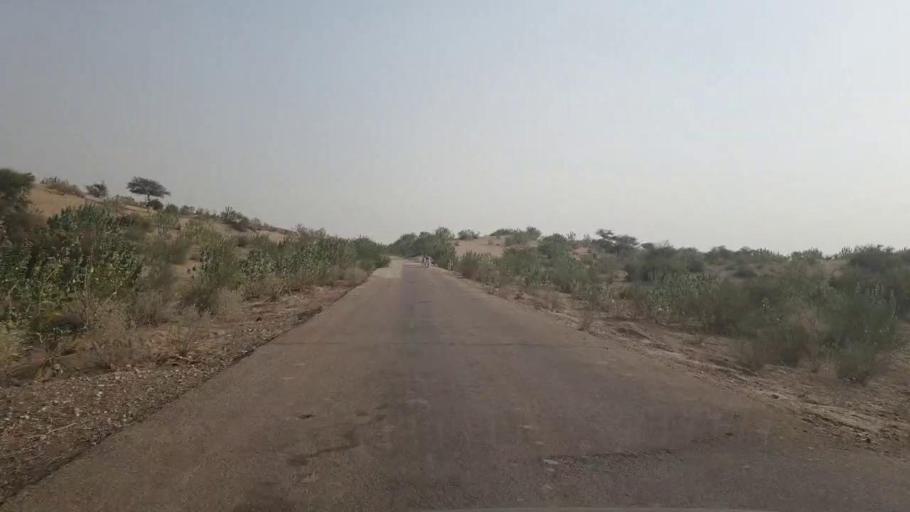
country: PK
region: Sindh
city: Chor
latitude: 25.5303
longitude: 69.9604
